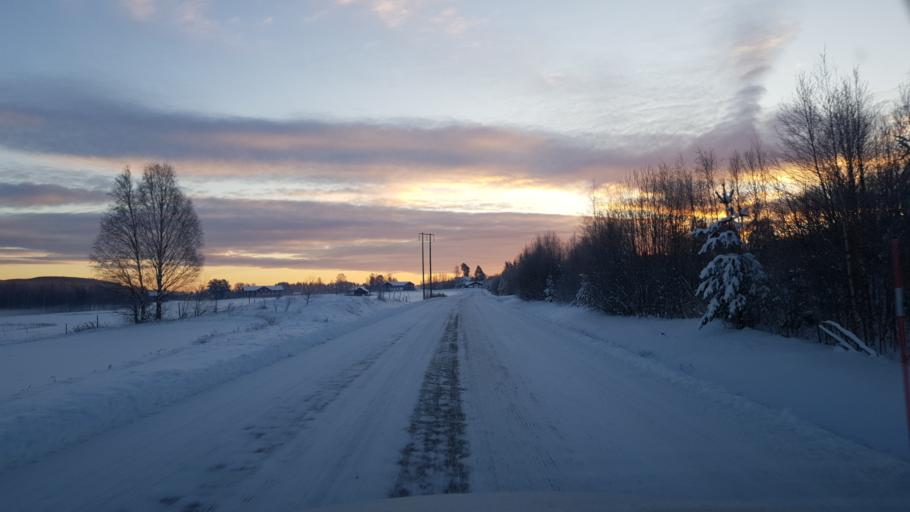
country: SE
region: Gaevleborg
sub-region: Ovanakers Kommun
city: Edsbyn
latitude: 61.3572
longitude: 15.9013
